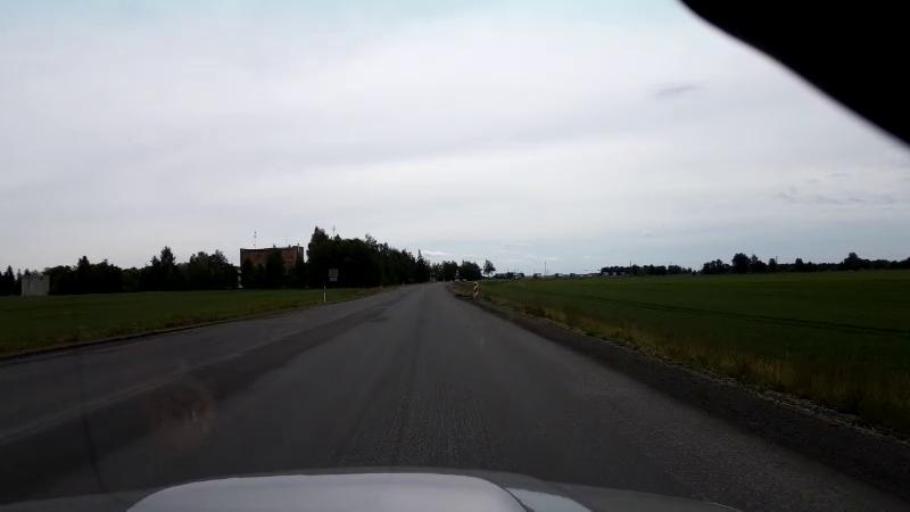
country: LV
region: Bauskas Rajons
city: Bauska
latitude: 56.3109
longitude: 24.3361
